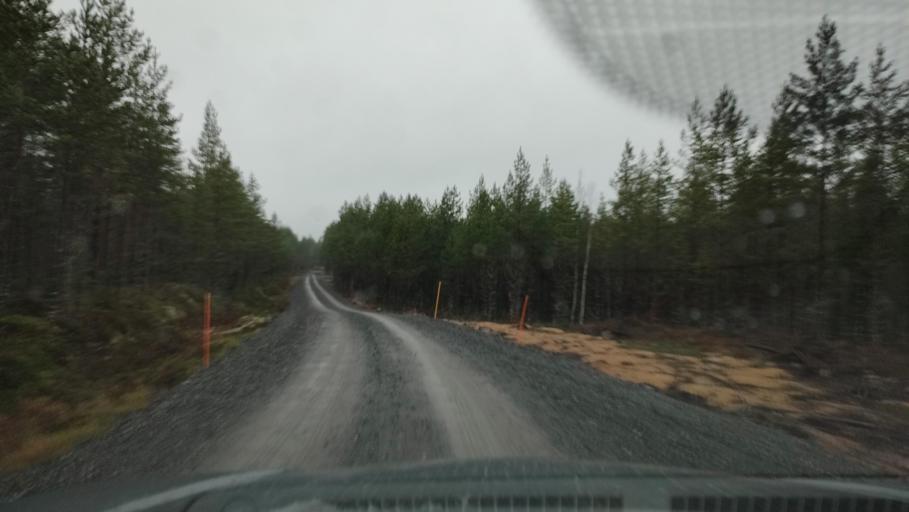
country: FI
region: Southern Ostrobothnia
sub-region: Suupohja
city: Karijoki
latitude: 62.1481
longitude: 21.6253
